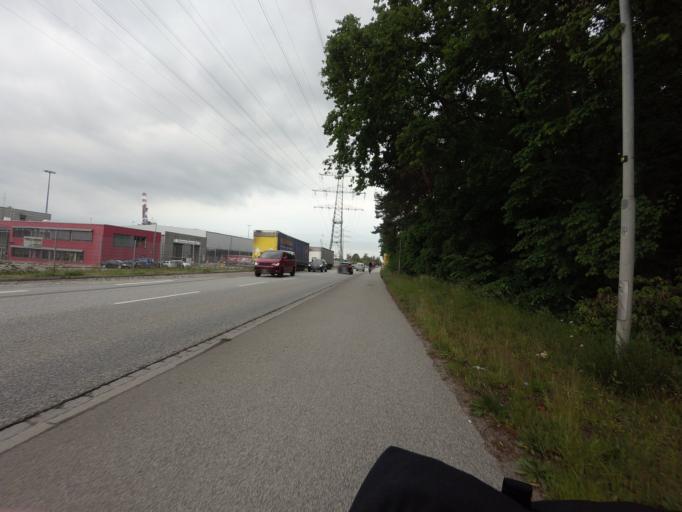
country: DE
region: Schleswig-Holstein
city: Ratekau
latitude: 53.9022
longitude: 10.7819
